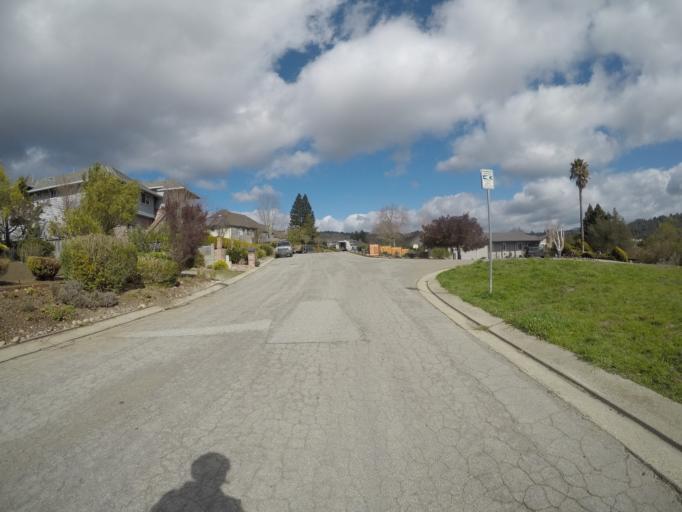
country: US
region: California
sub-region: Santa Cruz County
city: Scotts Valley
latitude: 37.0675
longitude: -122.0101
